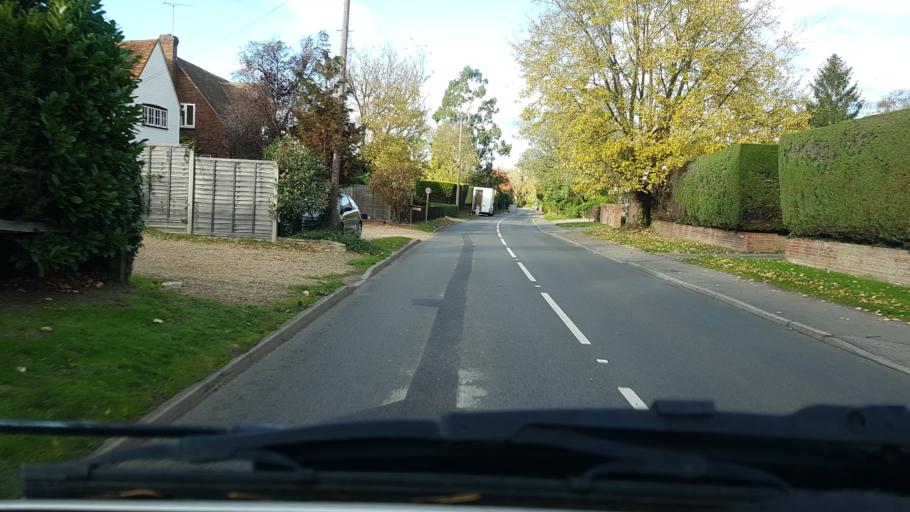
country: GB
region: England
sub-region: Surrey
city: Send
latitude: 51.2656
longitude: -0.5051
